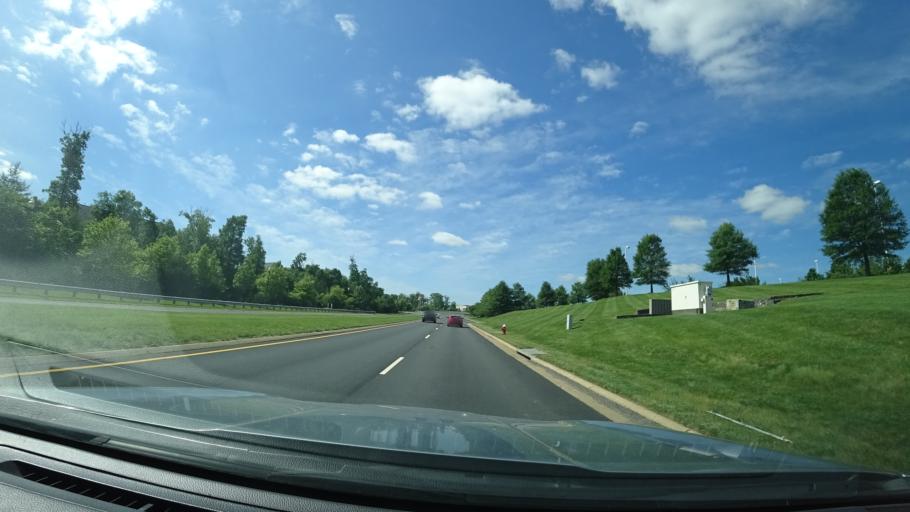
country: US
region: Virginia
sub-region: Loudoun County
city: Dulles Town Center
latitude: 39.0315
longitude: -77.4189
